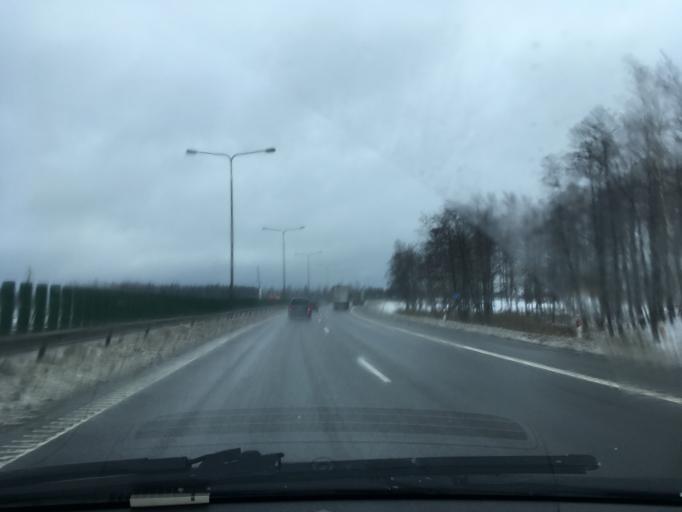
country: LT
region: Kauno apskritis
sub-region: Kauno rajonas
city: Karmelava
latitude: 54.9261
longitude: 24.0667
